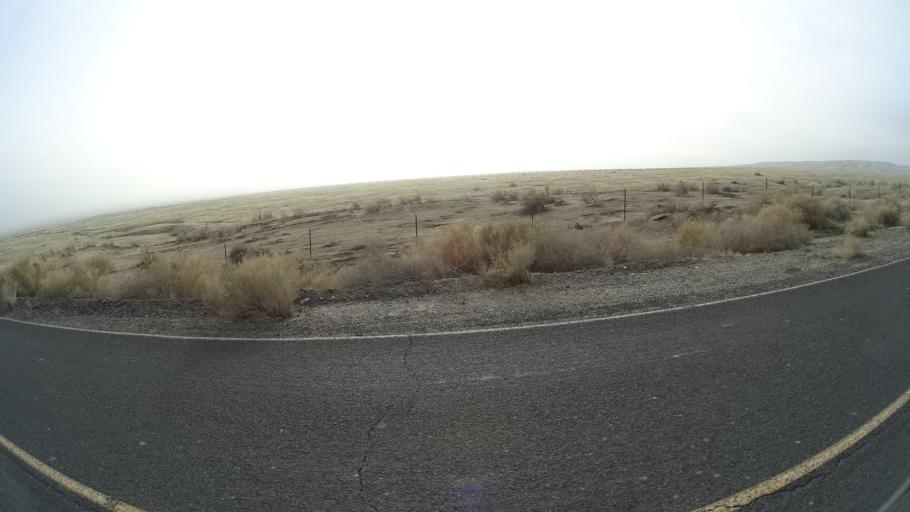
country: US
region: California
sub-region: Kern County
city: Ford City
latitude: 35.2387
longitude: -119.4493
